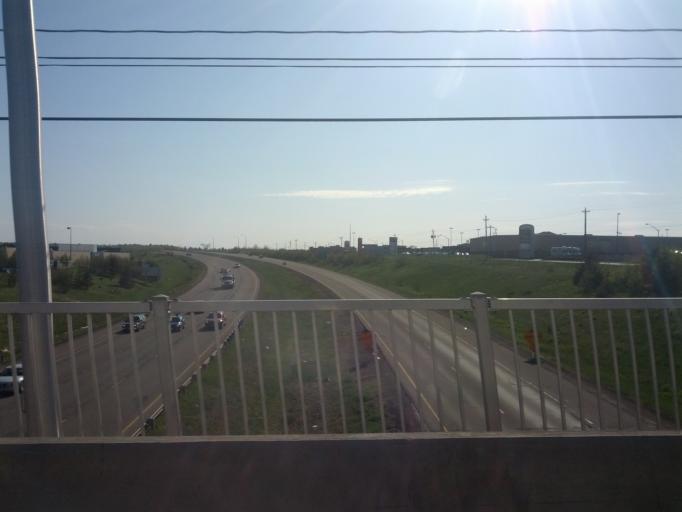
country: CA
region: New Brunswick
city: Moncton
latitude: 46.1167
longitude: -64.8268
